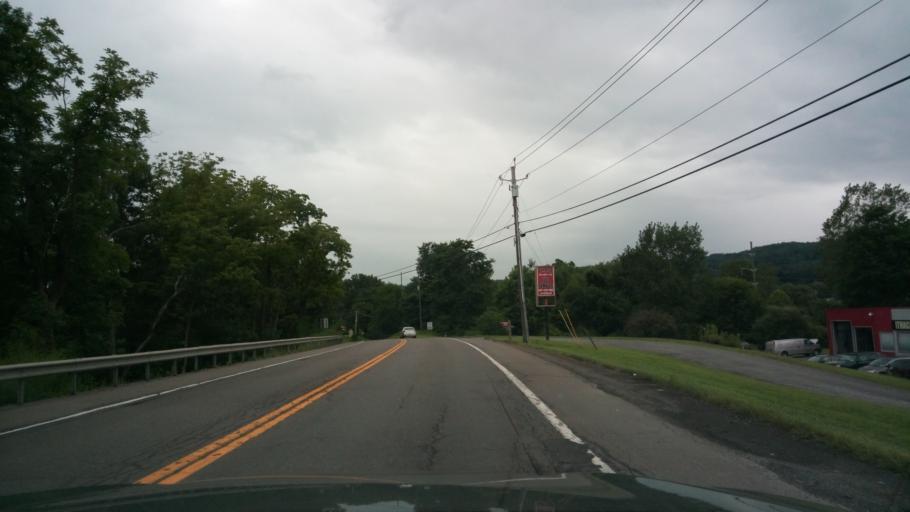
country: US
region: New York
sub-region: Tompkins County
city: South Hill
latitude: 42.4132
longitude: -76.5346
